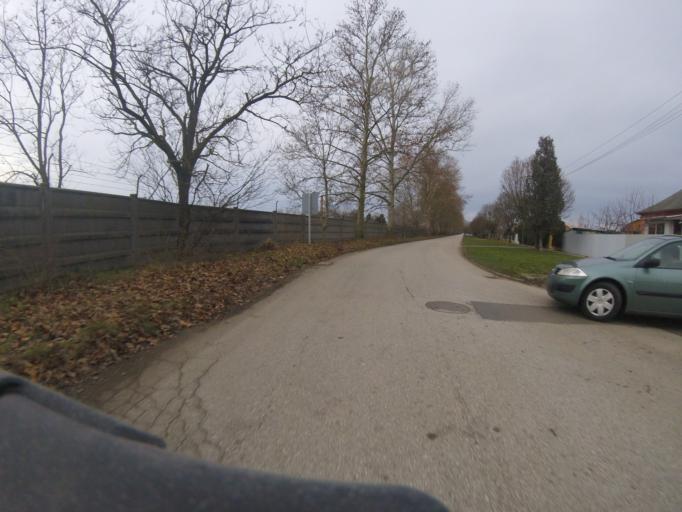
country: HU
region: Tolna
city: Dombovar
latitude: 46.3799
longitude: 18.1600
